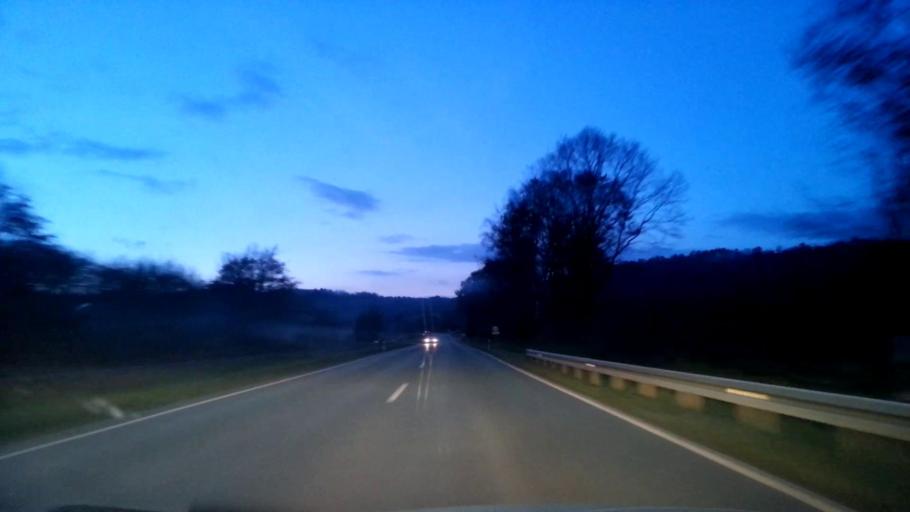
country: DE
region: Bavaria
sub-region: Upper Franconia
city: Reuth
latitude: 49.9698
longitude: 11.6886
